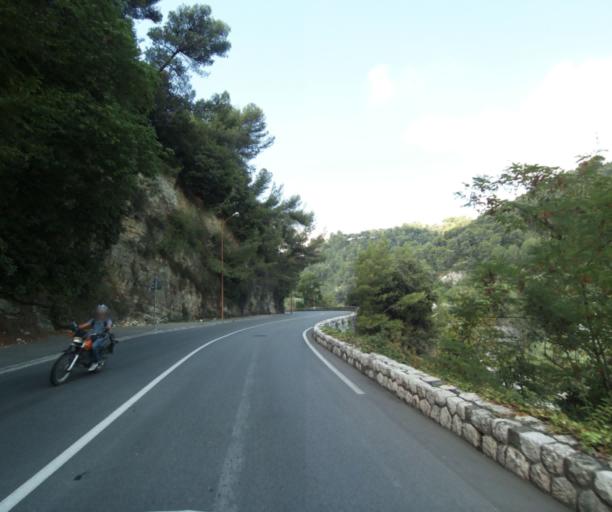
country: FR
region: Provence-Alpes-Cote d'Azur
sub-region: Departement des Alpes-Maritimes
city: La Trinite
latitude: 43.7454
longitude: 7.3167
